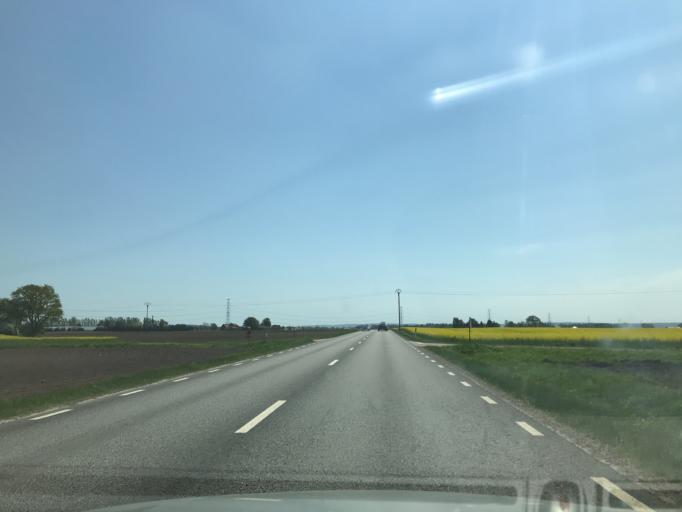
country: SE
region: Skane
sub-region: Astorps Kommun
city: Kvidinge
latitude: 56.2029
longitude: 13.0442
